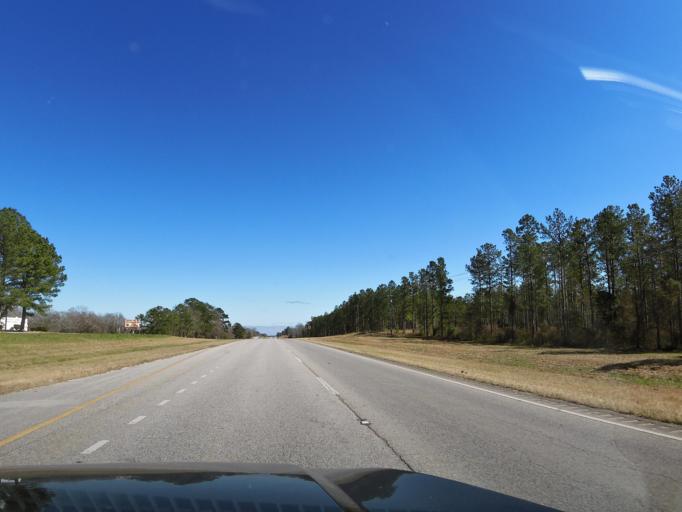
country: US
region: Alabama
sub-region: Bullock County
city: Union Springs
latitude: 32.1462
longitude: -85.6741
